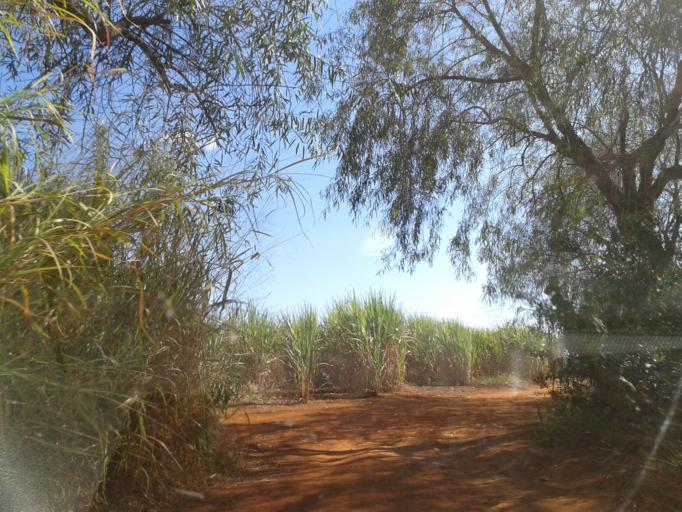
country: BR
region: Minas Gerais
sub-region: Centralina
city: Centralina
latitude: -18.5915
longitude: -49.2739
